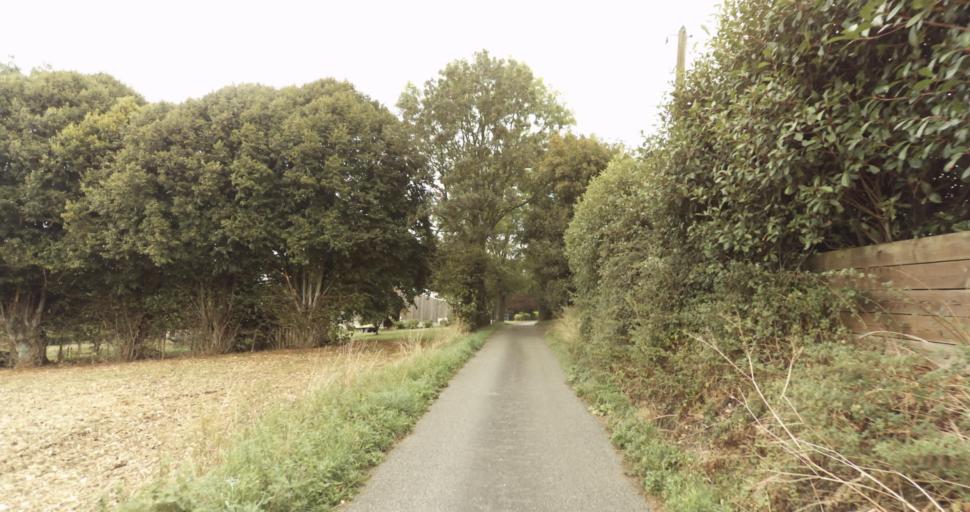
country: FR
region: Lower Normandy
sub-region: Departement de l'Orne
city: Vimoutiers
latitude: 48.8618
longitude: 0.2311
